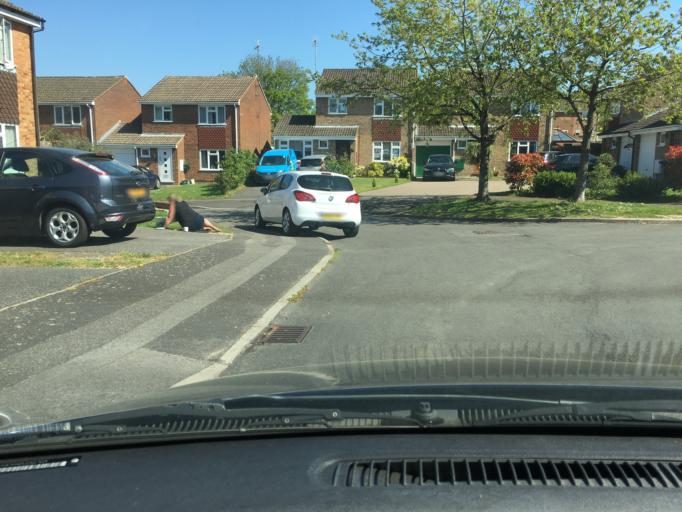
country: GB
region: England
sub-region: Hampshire
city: Yateley
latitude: 51.3335
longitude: -0.8387
